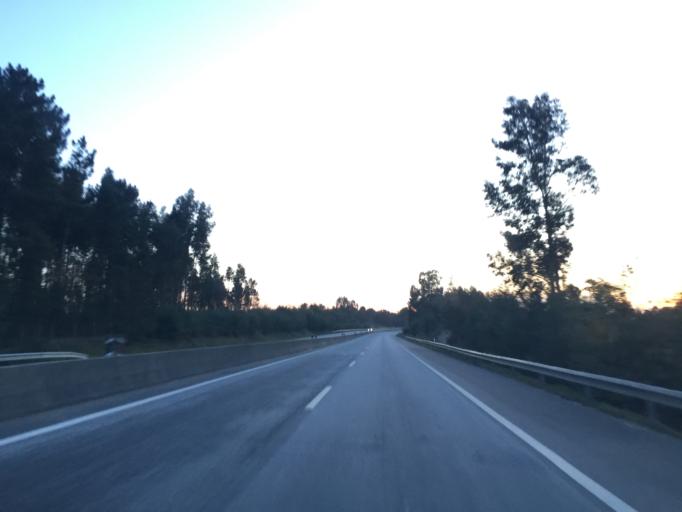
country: PT
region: Viseu
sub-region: Santa Comba Dao
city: Santa Comba Dao
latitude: 40.4034
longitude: -8.0769
